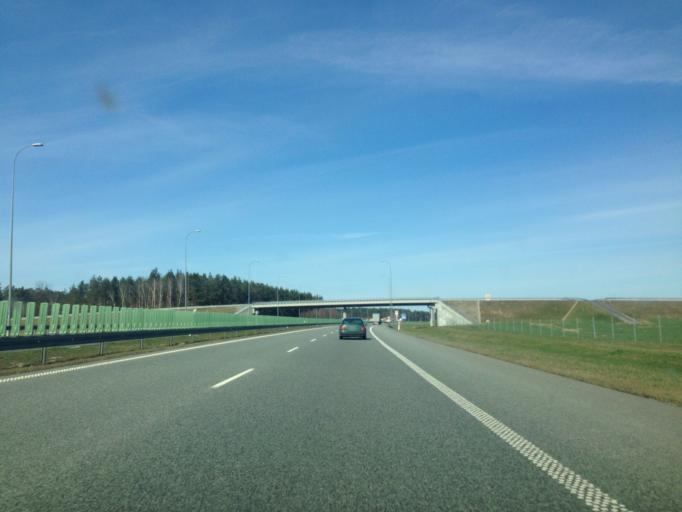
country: PL
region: Pomeranian Voivodeship
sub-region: Powiat starogardzki
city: Bobowo
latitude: 53.8814
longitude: 18.6275
